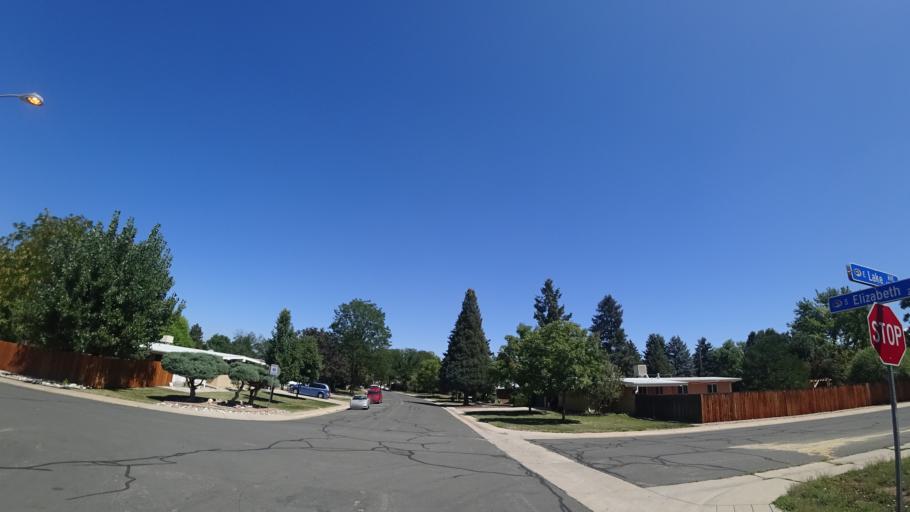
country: US
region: Colorado
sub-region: Arapahoe County
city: Greenwood Village
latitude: 39.6072
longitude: -104.9561
